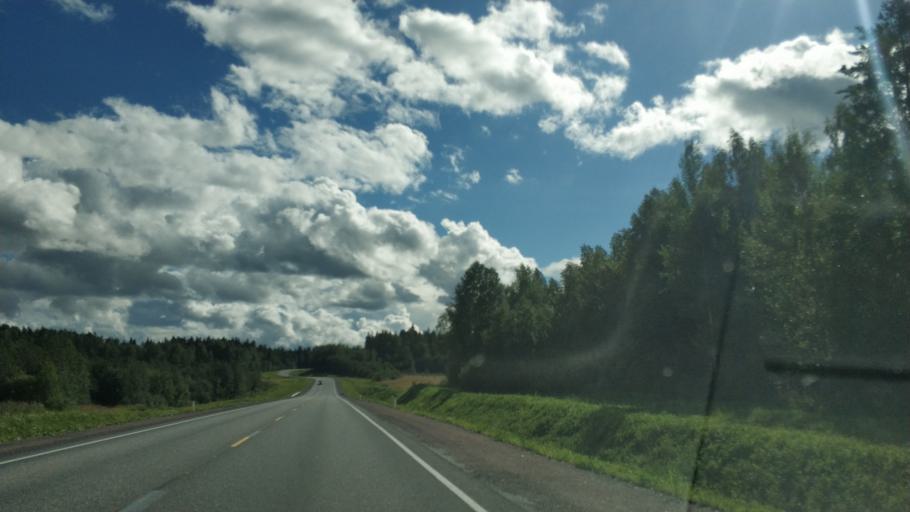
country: RU
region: Republic of Karelia
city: Ruskeala
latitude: 61.8745
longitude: 30.6480
